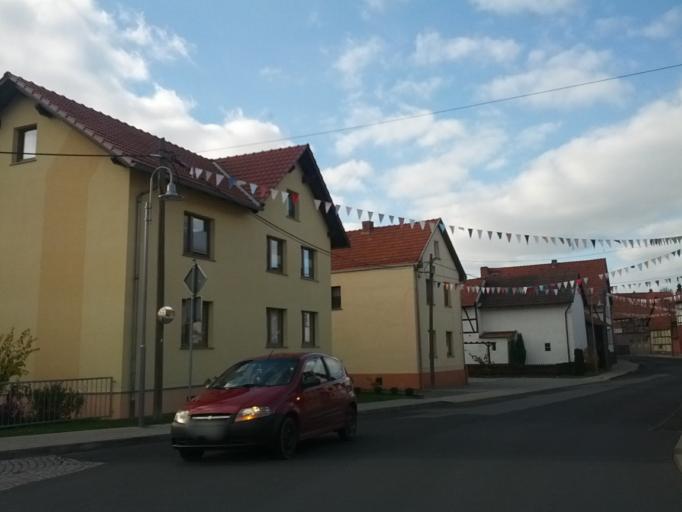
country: DE
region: Thuringia
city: Marksuhl
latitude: 50.9291
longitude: 10.1563
